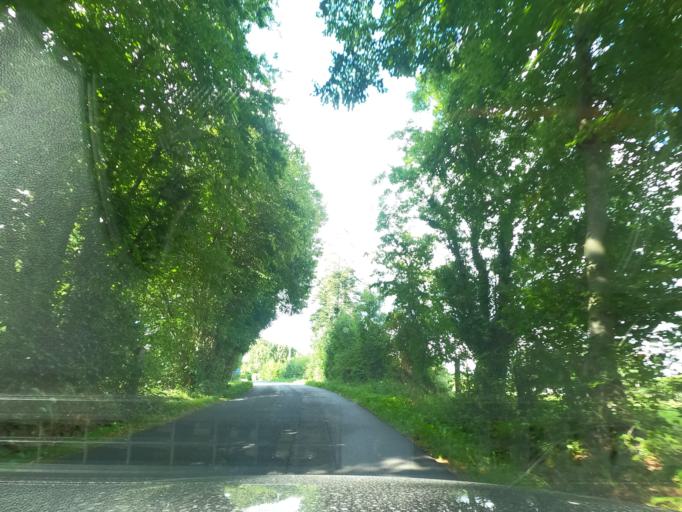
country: FR
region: Lower Normandy
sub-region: Departement de l'Orne
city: Gace
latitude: 48.7842
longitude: 0.2604
